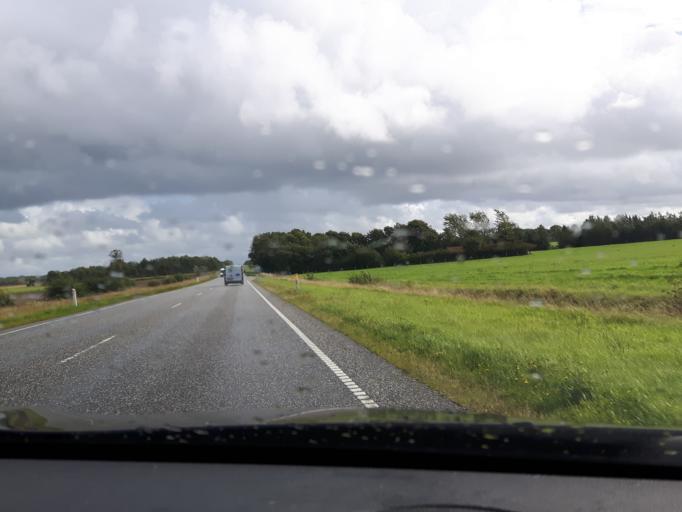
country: DK
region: Central Jutland
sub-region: Holstebro Kommune
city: Holstebro
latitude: 56.3155
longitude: 8.6865
